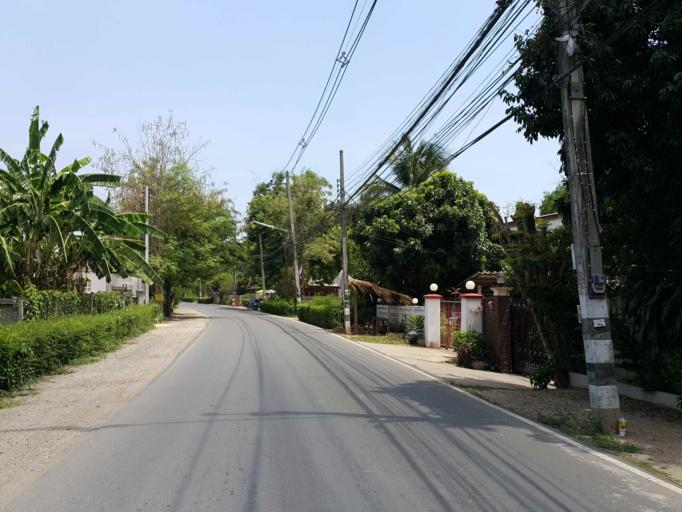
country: TH
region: Chiang Mai
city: Chiang Mai
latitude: 18.8351
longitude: 98.9920
